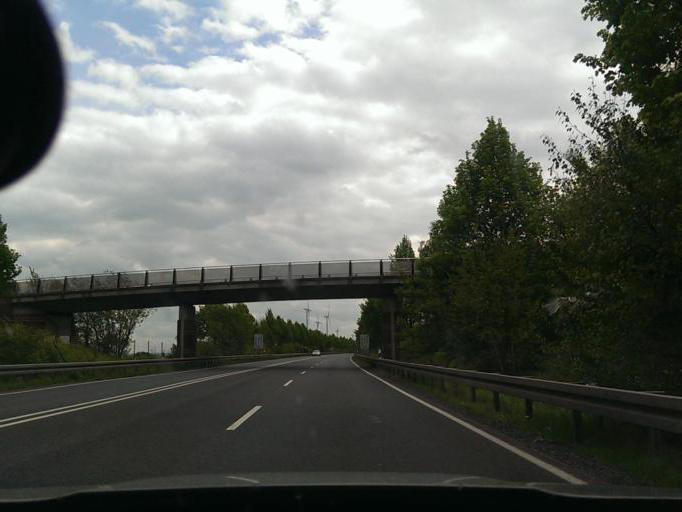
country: DE
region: Lower Saxony
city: Pattensen
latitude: 52.2638
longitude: 9.7817
